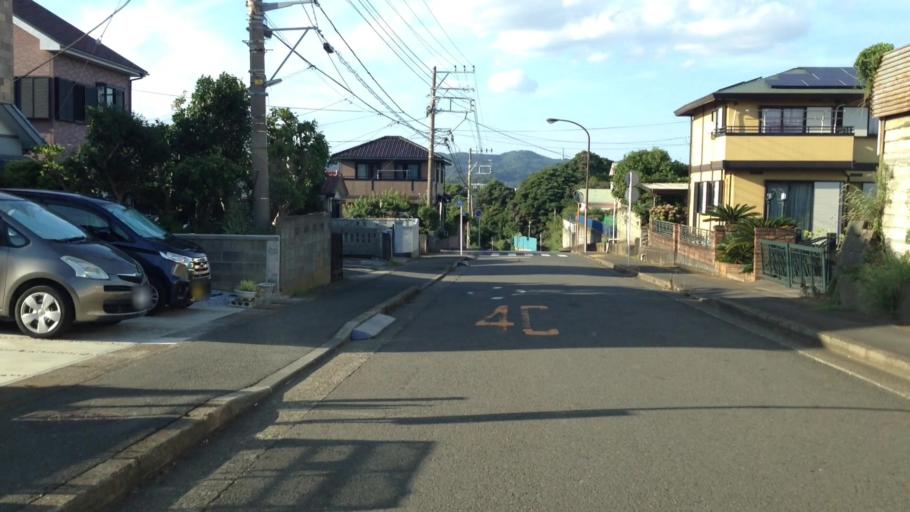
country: JP
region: Kanagawa
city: Miura
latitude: 35.2039
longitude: 139.6153
